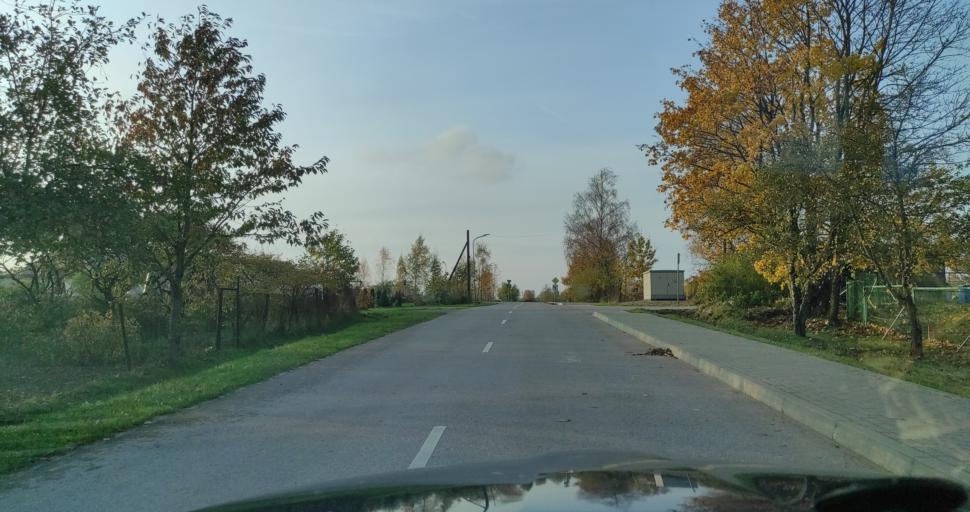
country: LV
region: Vainode
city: Vainode
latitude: 56.4206
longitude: 21.8511
